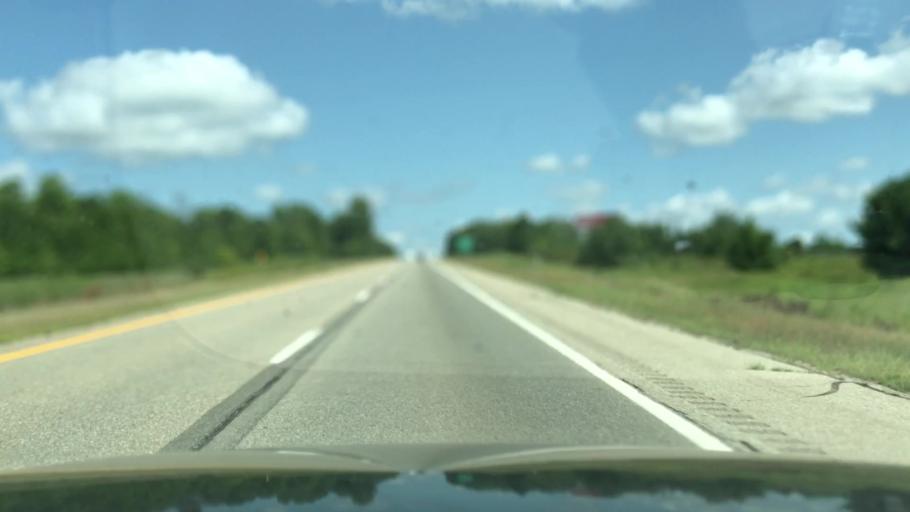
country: US
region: Michigan
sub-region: Mecosta County
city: Big Rapids
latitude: 43.7199
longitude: -85.5311
